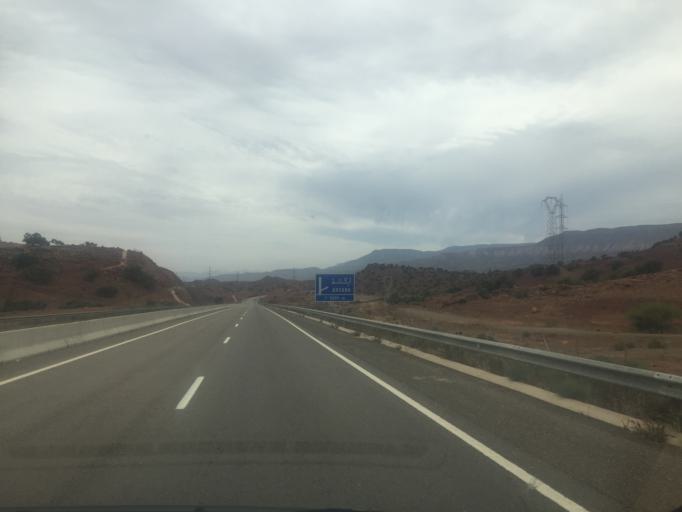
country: MA
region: Marrakech-Tensift-Al Haouz
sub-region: Chichaoua
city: Timezgadiouine
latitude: 30.8683
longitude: -9.0887
